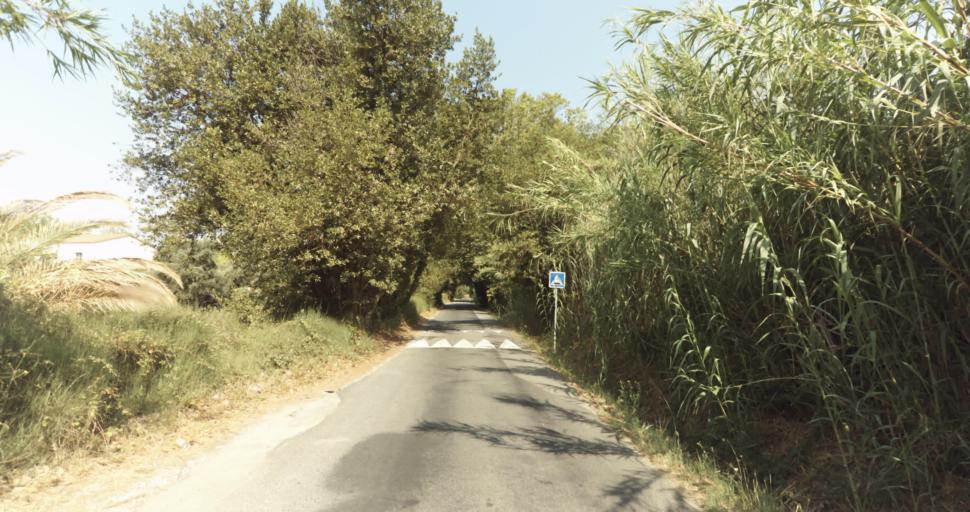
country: FR
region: Languedoc-Roussillon
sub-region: Departement des Pyrenees-Orientales
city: Latour-Bas-Elne
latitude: 42.6149
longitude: 2.9867
